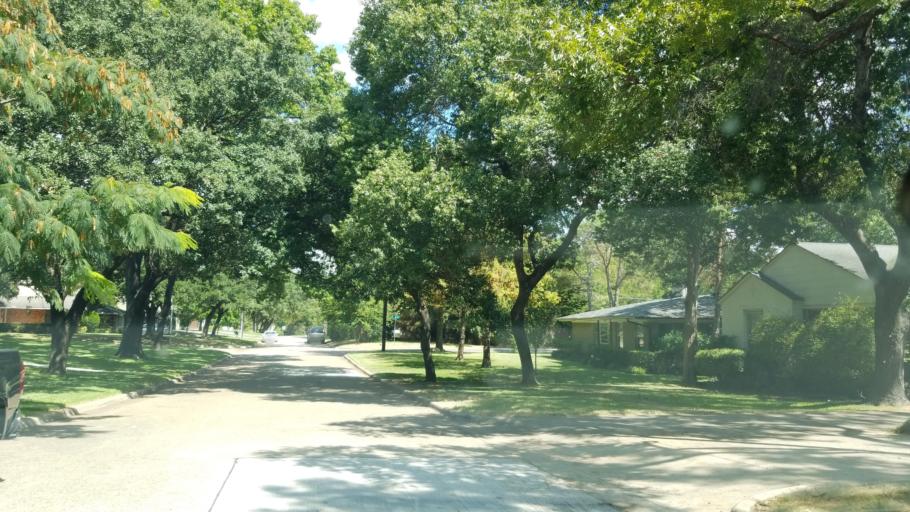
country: US
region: Texas
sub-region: Dallas County
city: Dallas
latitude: 32.7606
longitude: -96.8343
